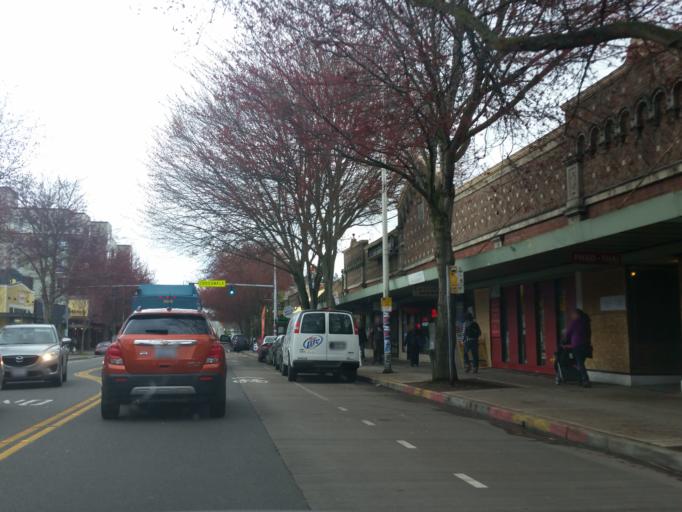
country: US
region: Washington
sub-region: King County
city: Shoreline
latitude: 47.6908
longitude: -122.3553
